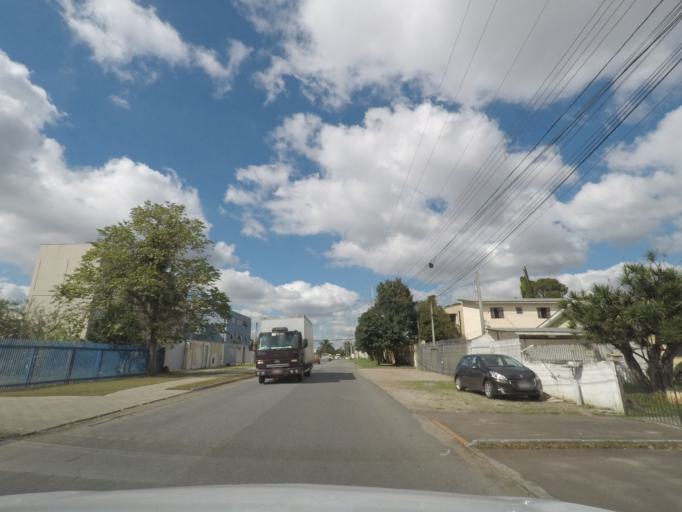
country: BR
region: Parana
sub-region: Sao Jose Dos Pinhais
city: Sao Jose dos Pinhais
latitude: -25.5108
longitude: -49.2202
